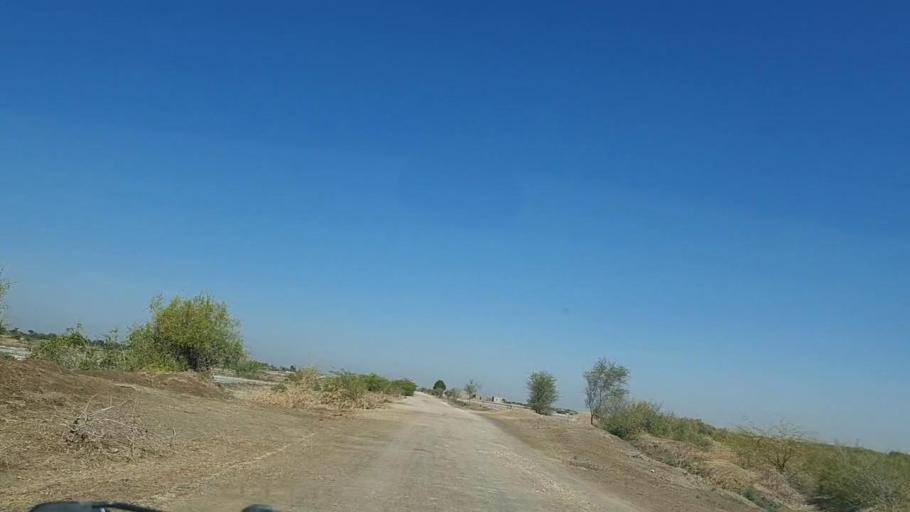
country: PK
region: Sindh
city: Dhoro Naro
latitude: 25.4780
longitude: 69.5272
